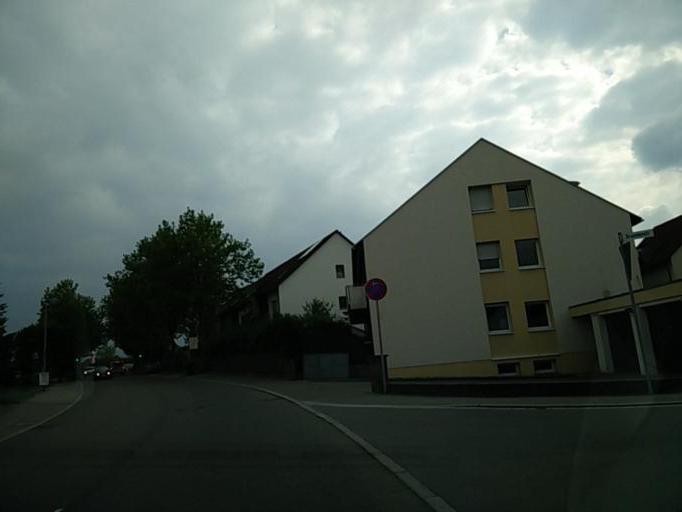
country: DE
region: Baden-Wuerttemberg
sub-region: Regierungsbezirk Stuttgart
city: Holzgerlingen
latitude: 48.6329
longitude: 9.0145
